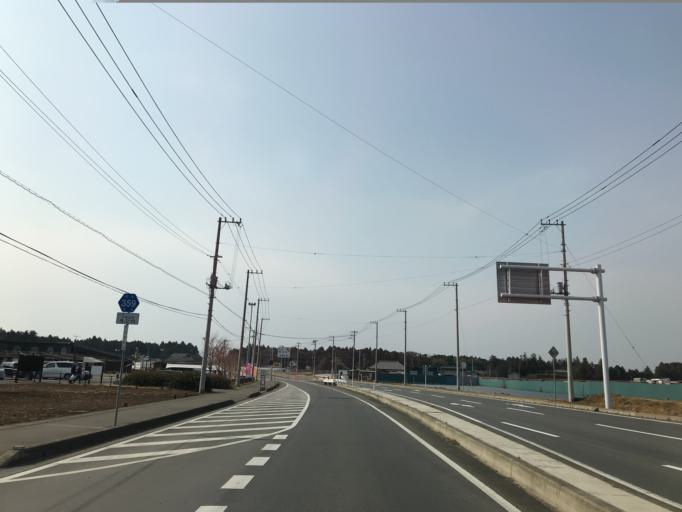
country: JP
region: Ibaraki
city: Okunoya
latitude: 36.1811
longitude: 140.4024
